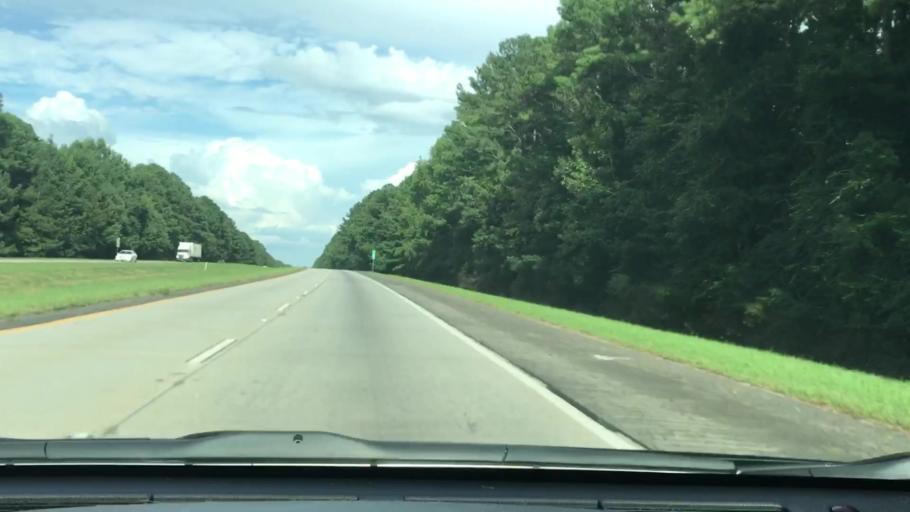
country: US
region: Georgia
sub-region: Taliaferro County
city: Crawfordville
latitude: 33.5277
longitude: -82.9497
